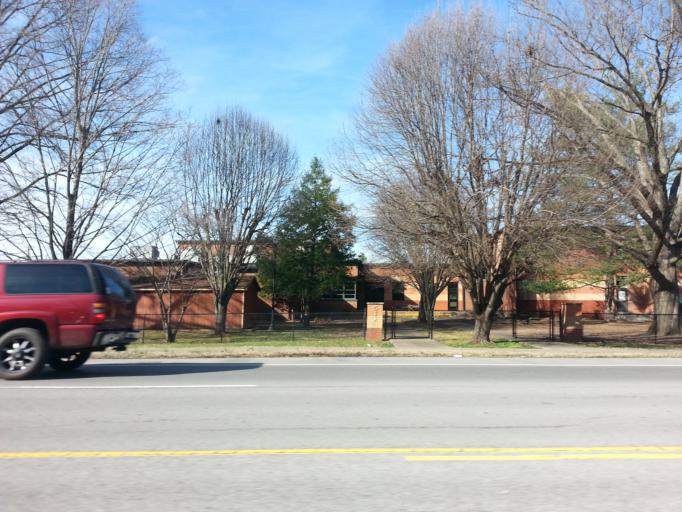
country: US
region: Tennessee
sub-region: Rutherford County
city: Murfreesboro
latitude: 35.8374
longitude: -86.3842
